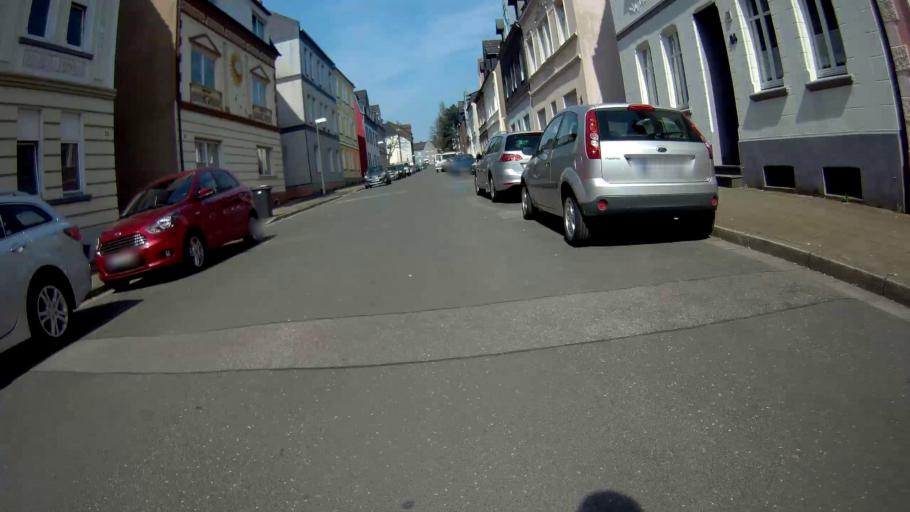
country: DE
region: North Rhine-Westphalia
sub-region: Regierungsbezirk Munster
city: Gladbeck
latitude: 51.5719
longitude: 7.0420
